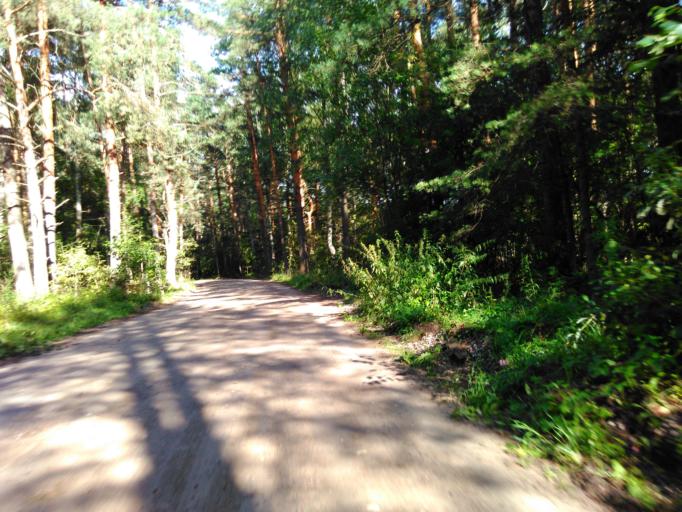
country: RU
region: Vladimir
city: Pokrov
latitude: 55.9708
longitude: 39.1110
